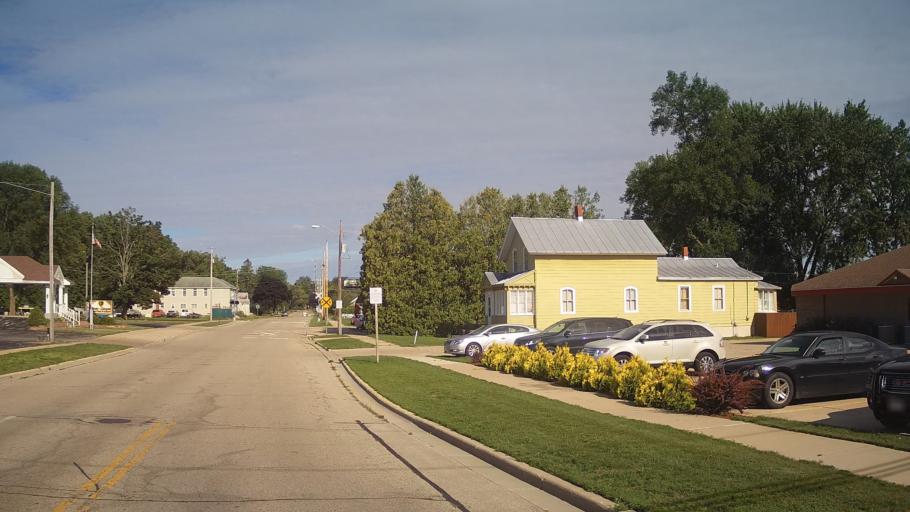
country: US
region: Wisconsin
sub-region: Oconto County
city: Oconto
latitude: 44.8905
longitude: -87.8827
